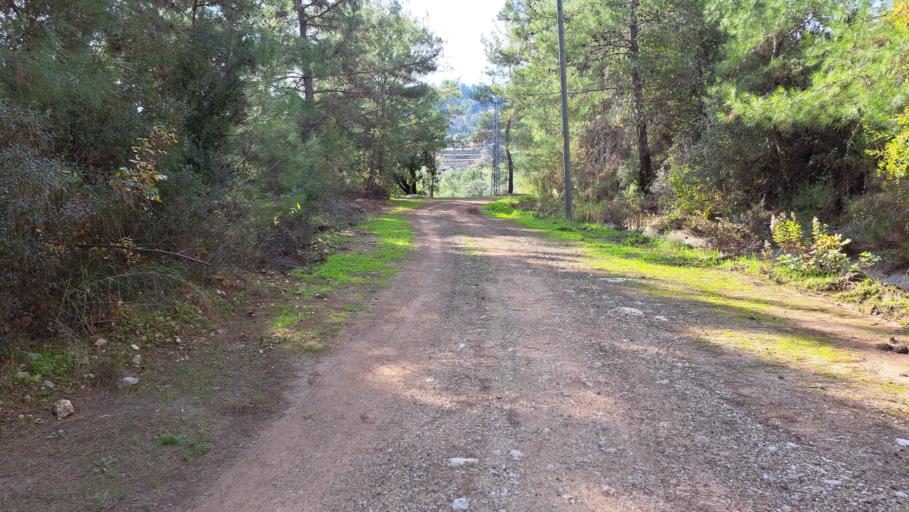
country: TR
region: Antalya
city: Tekirova
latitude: 36.3958
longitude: 30.4304
